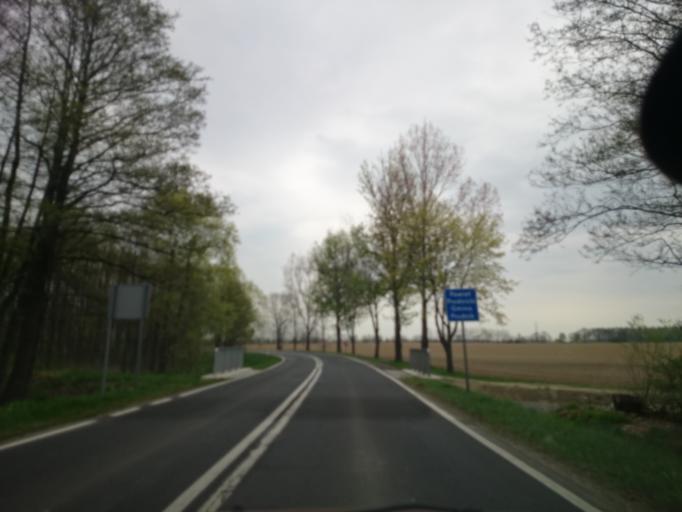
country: PL
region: Opole Voivodeship
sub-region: Powiat prudnicki
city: Moszczanka
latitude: 50.3235
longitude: 17.4560
